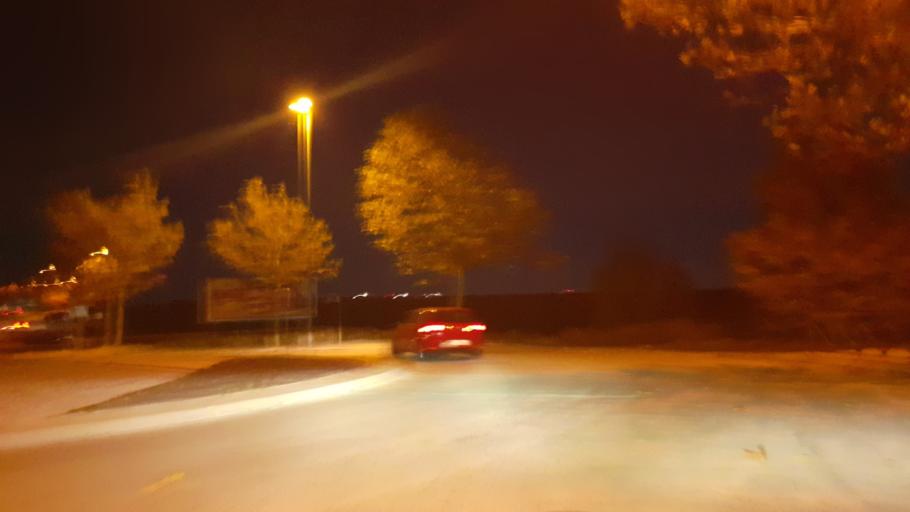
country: ES
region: Madrid
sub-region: Provincia de Madrid
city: Paracuellos de Jarama
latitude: 40.5084
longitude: -3.5110
